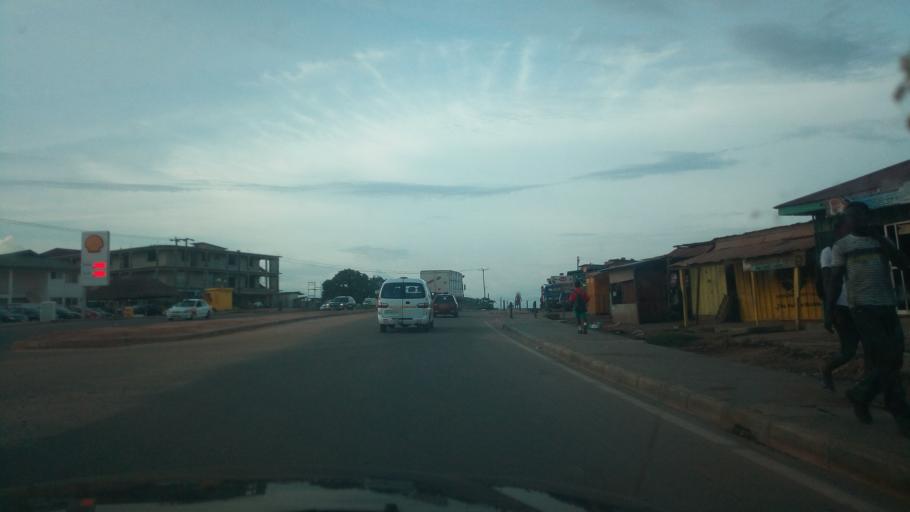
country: GH
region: Western
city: Takoradi
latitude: 4.9139
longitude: -1.7934
